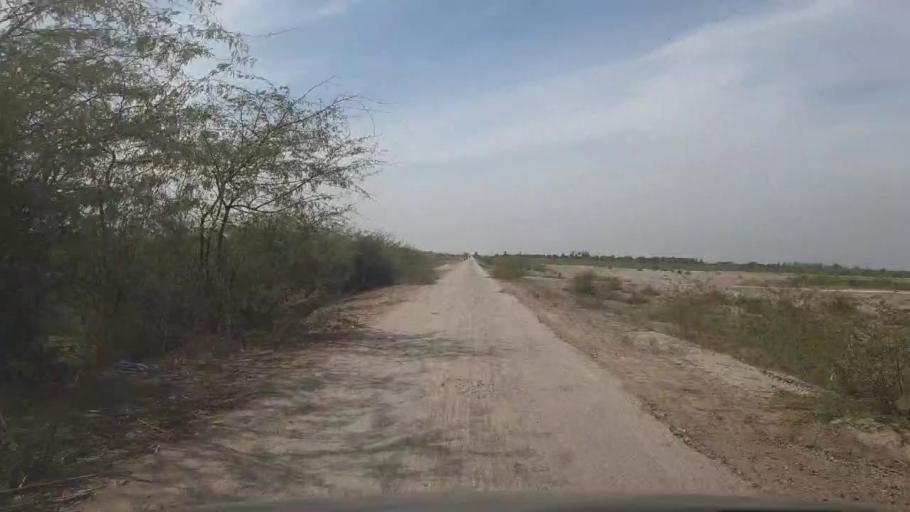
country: PK
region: Sindh
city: Kunri
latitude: 25.2121
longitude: 69.6167
